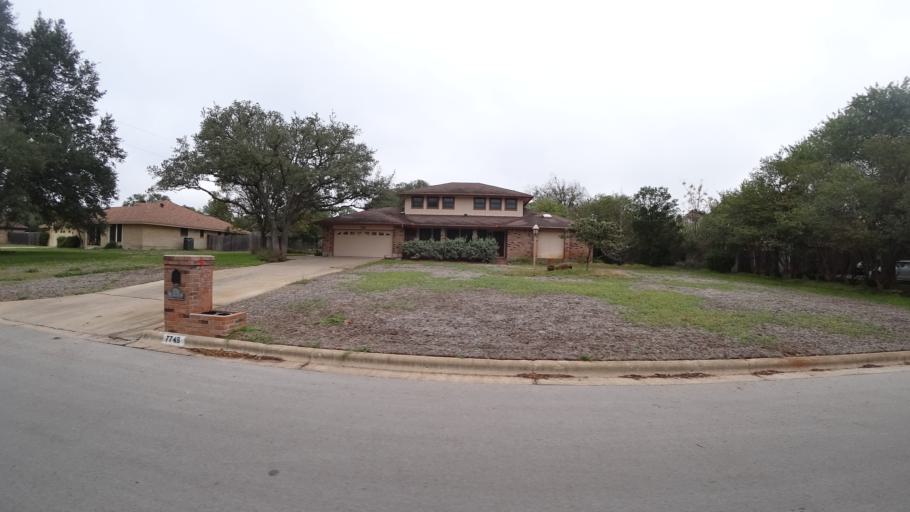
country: US
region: Texas
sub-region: Travis County
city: Shady Hollow
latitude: 30.2156
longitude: -97.9100
